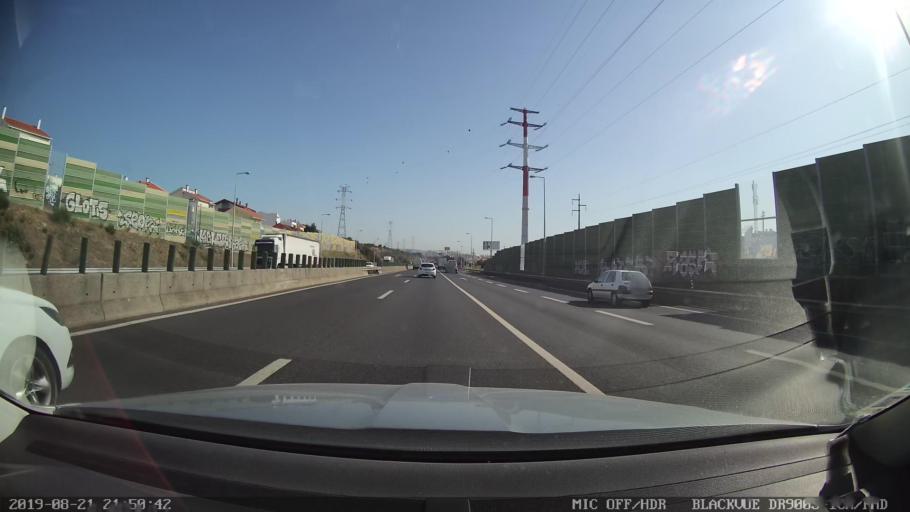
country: PT
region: Lisbon
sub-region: Loures
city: Santa Iria da Azoia
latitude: 38.8441
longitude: -9.0909
